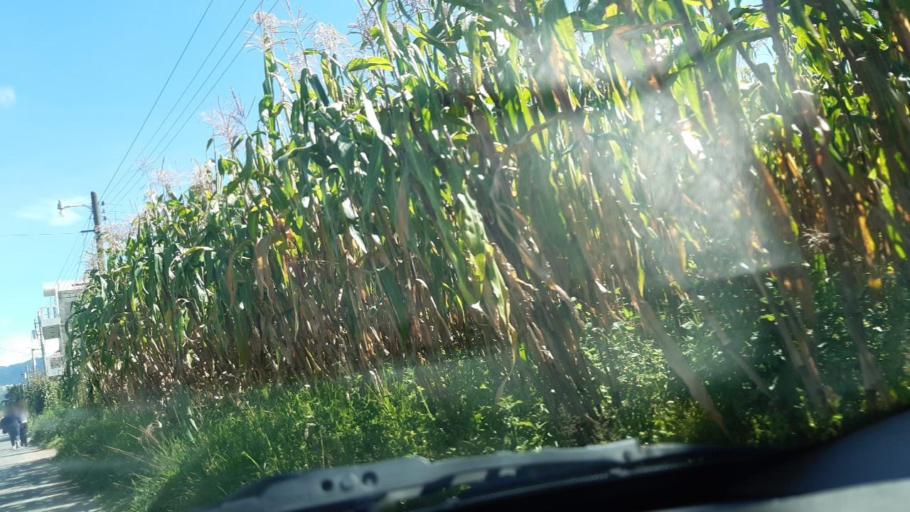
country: GT
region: Quetzaltenango
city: Salcaja
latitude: 14.8836
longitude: -91.4510
